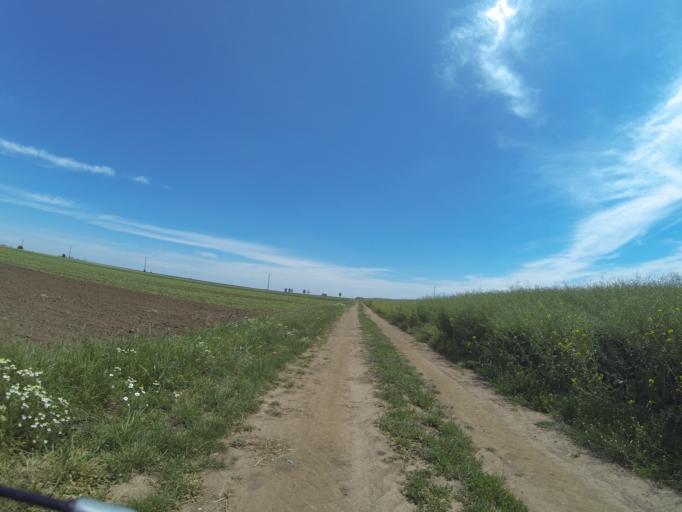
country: RO
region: Dolj
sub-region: Comuna Diosti
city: Radomir
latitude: 44.1473
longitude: 24.1511
